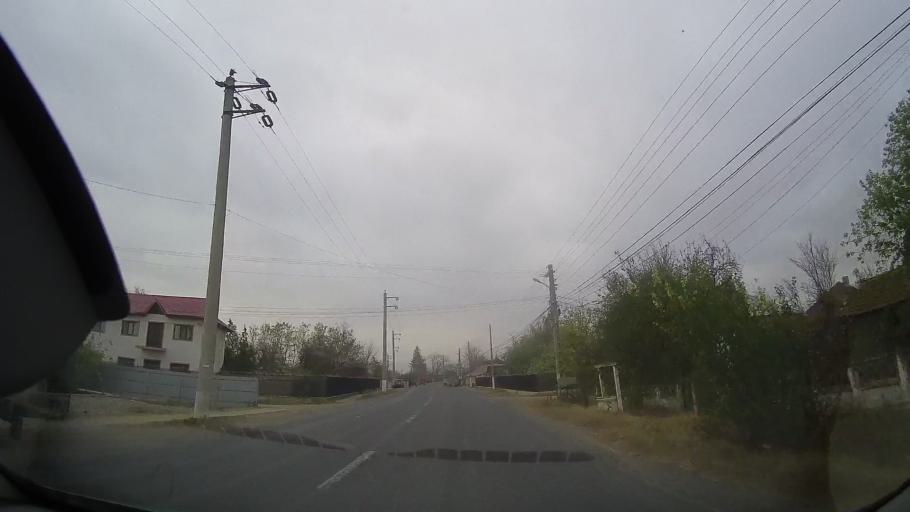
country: RO
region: Buzau
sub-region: Comuna Padina
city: Padina
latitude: 44.8228
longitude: 27.1151
